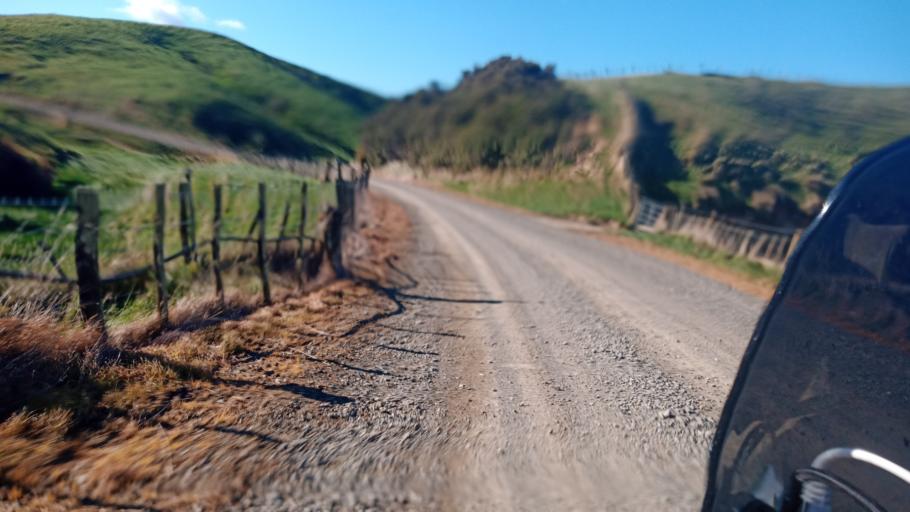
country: NZ
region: Hawke's Bay
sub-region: Wairoa District
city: Wairoa
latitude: -38.7487
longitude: 177.2765
